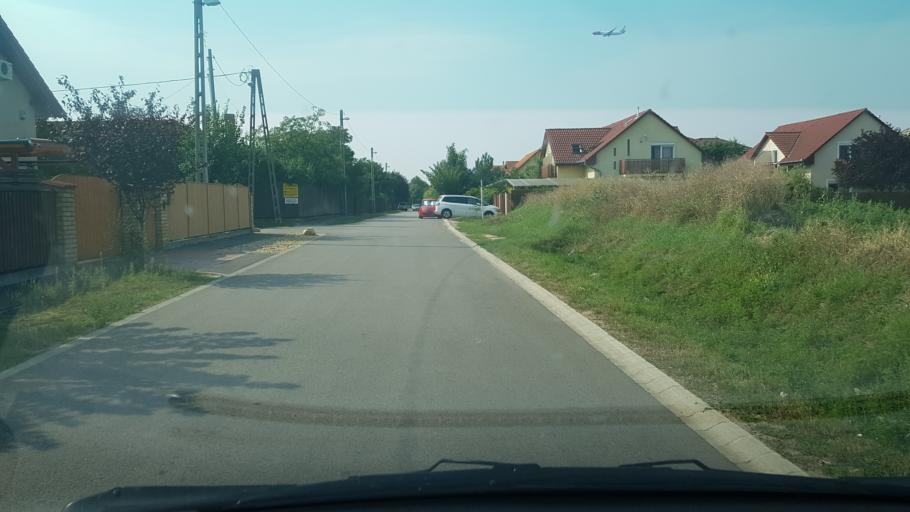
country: HU
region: Budapest
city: Budapest XVII. keruelet
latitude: 47.4714
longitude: 19.2327
